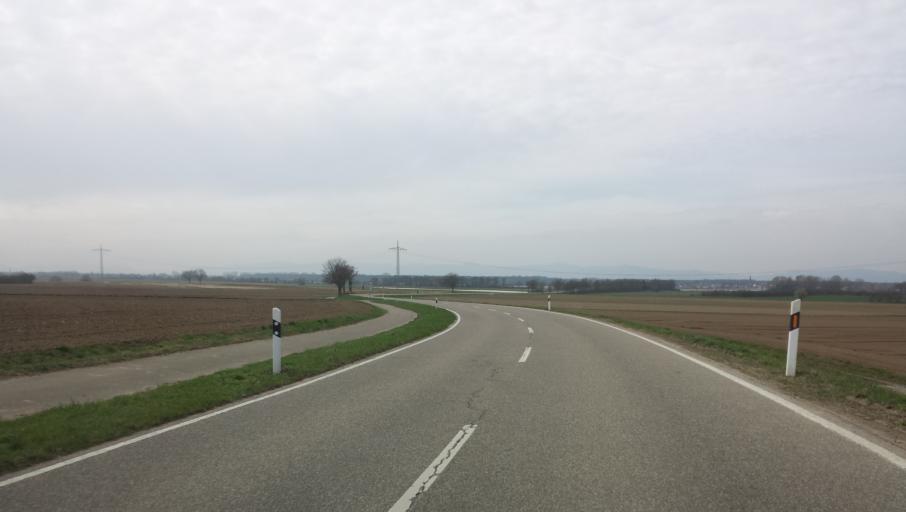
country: DE
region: Rheinland-Pfalz
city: Dudenhofen
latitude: 49.2849
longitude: 8.3817
